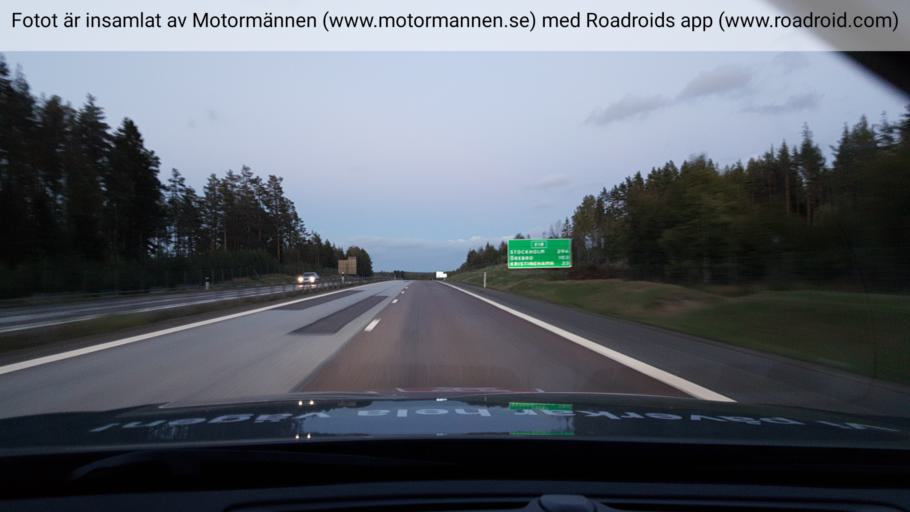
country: SE
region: Vaermland
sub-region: Karlstads Kommun
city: Skattkarr
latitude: 59.4036
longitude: 13.6253
